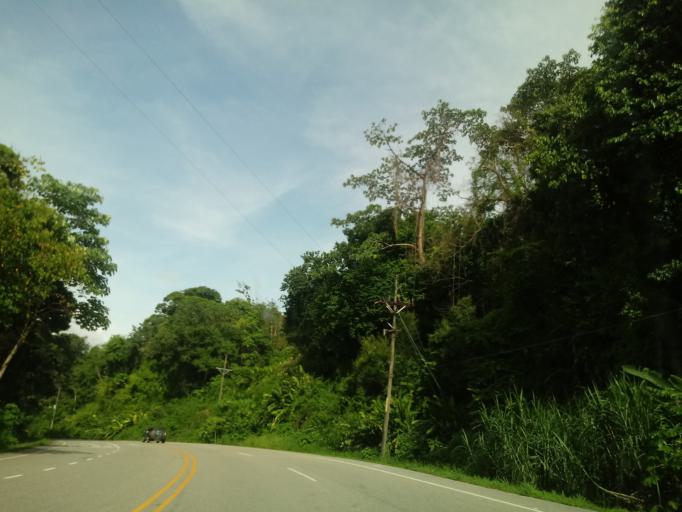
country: CR
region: San Jose
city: Daniel Flores
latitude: 9.2000
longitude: -83.7890
